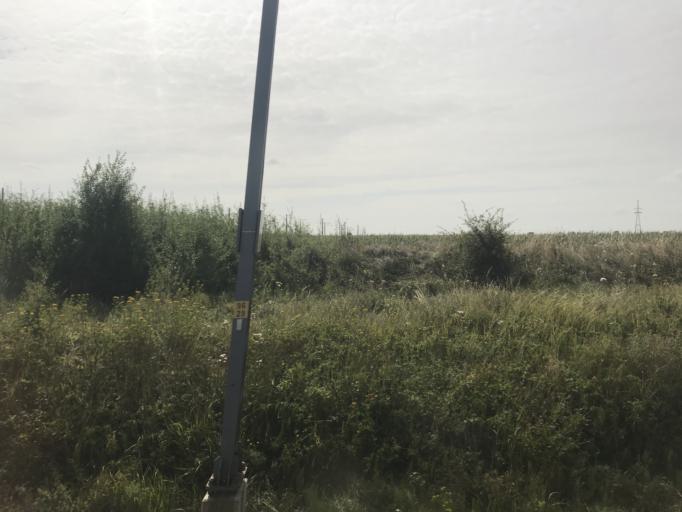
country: PL
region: Kujawsko-Pomorskie
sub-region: Powiat inowroclawski
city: Inowroclaw
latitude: 52.7851
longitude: 18.1947
